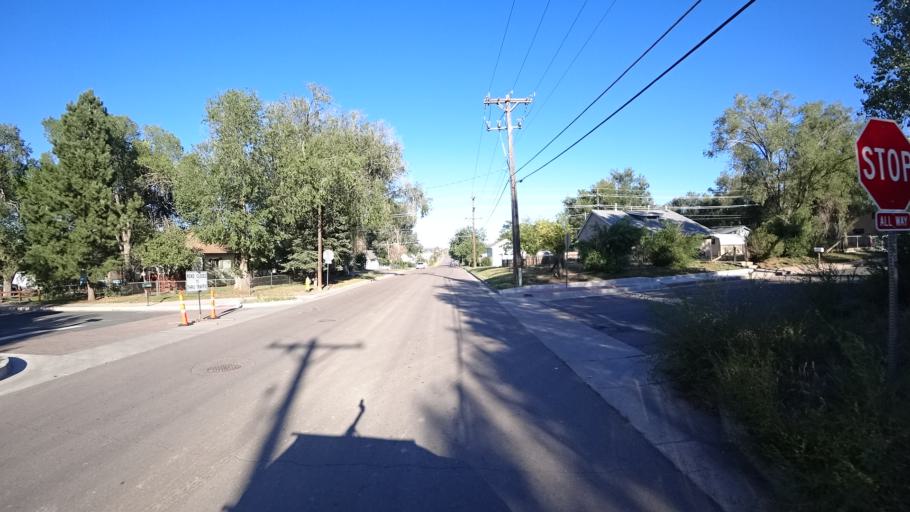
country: US
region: Colorado
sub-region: El Paso County
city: Colorado Springs
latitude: 38.8354
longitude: -104.8658
